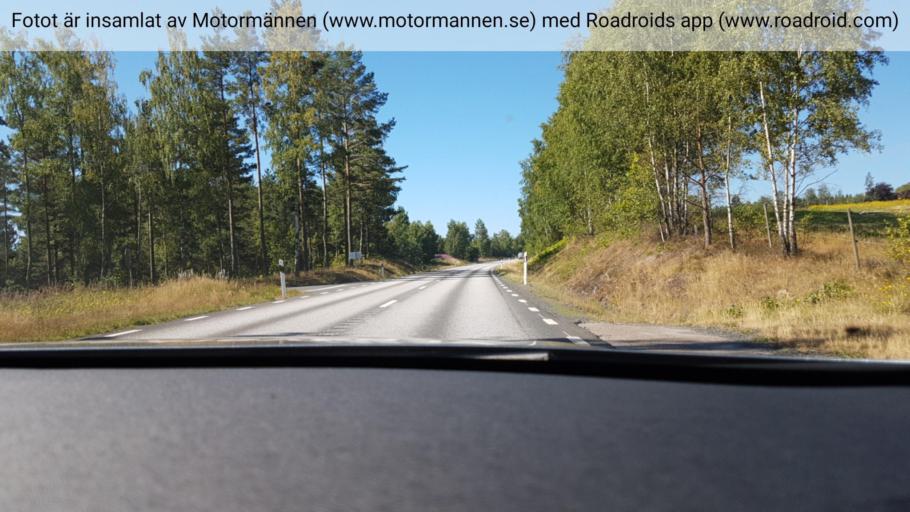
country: SE
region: Joenkoeping
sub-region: Habo Kommun
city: Habo
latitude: 58.0334
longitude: 14.1737
